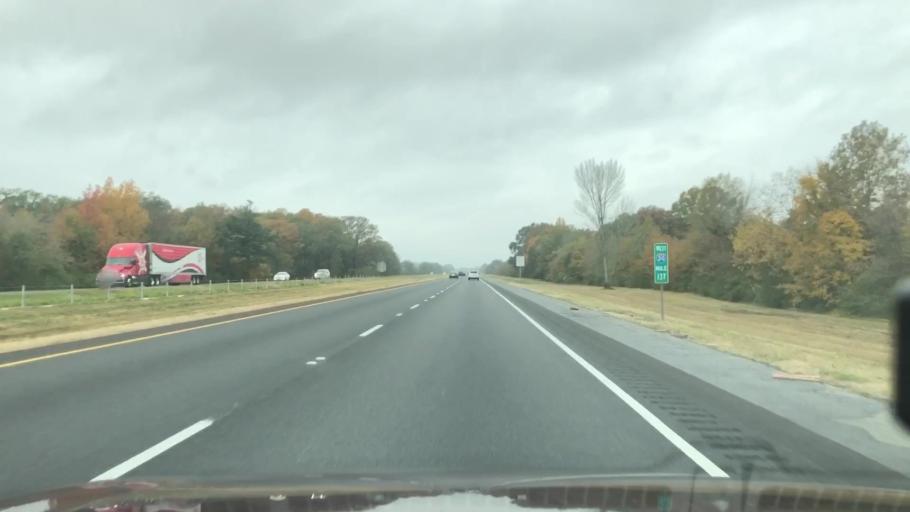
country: US
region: Louisiana
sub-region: Richland Parish
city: Rayville
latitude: 32.4595
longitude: -91.7754
